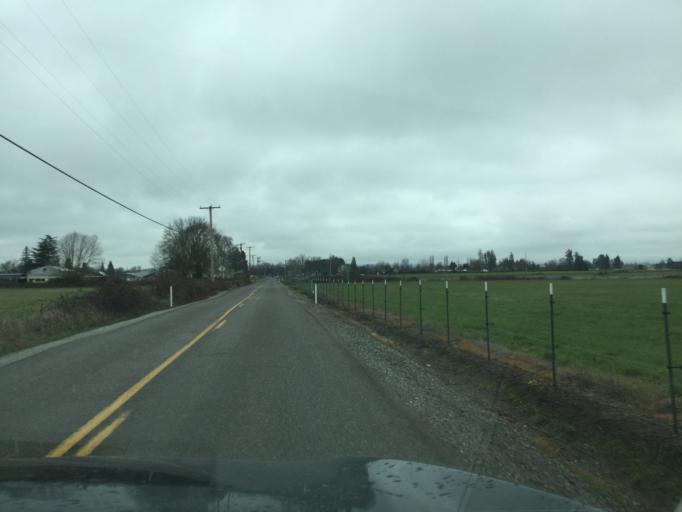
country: US
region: Oregon
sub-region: Jackson County
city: Central Point
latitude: 42.3898
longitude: -122.9484
